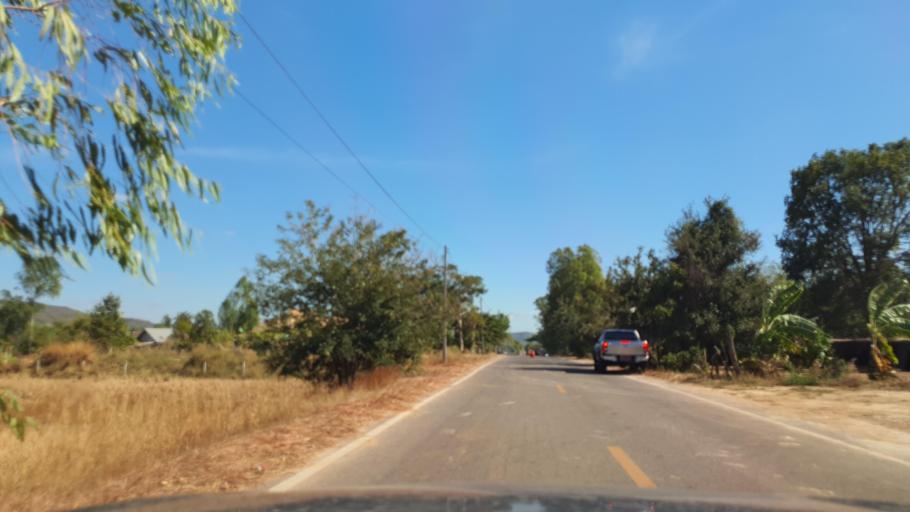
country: TH
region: Kalasin
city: Khao Wong
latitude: 16.7251
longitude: 104.1021
